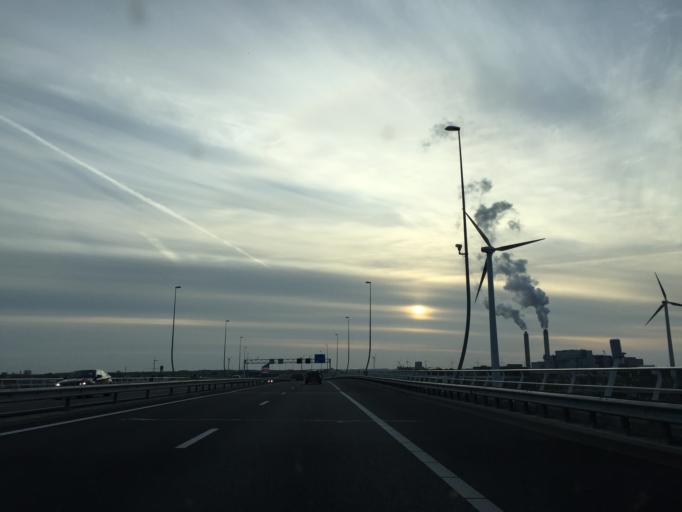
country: NL
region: North Holland
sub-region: Gemeente Zaanstad
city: Zaandam
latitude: 52.3927
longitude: 4.8090
